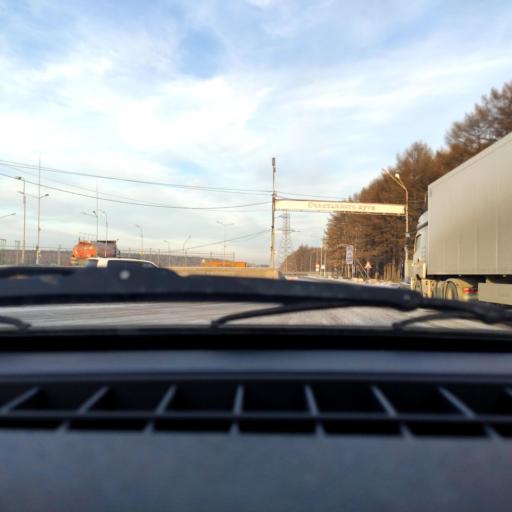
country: RU
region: Bashkortostan
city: Avdon
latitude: 54.6727
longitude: 55.7852
